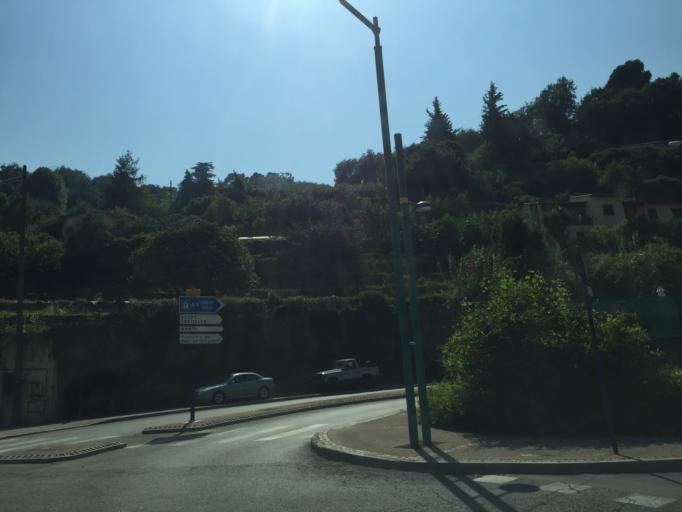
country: FR
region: Provence-Alpes-Cote d'Azur
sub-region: Departement des Alpes-Maritimes
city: Menton
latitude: 43.7949
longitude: 7.4904
